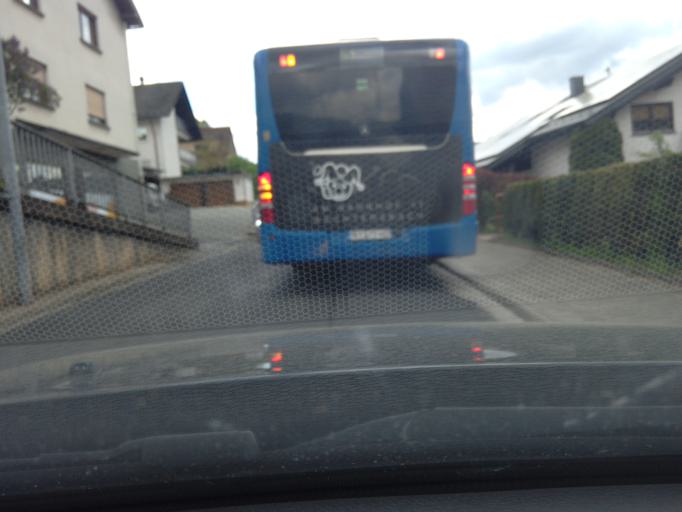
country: DE
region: Bavaria
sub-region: Regierungsbezirk Unterfranken
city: Frammersbach
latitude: 50.1261
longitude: 9.4801
